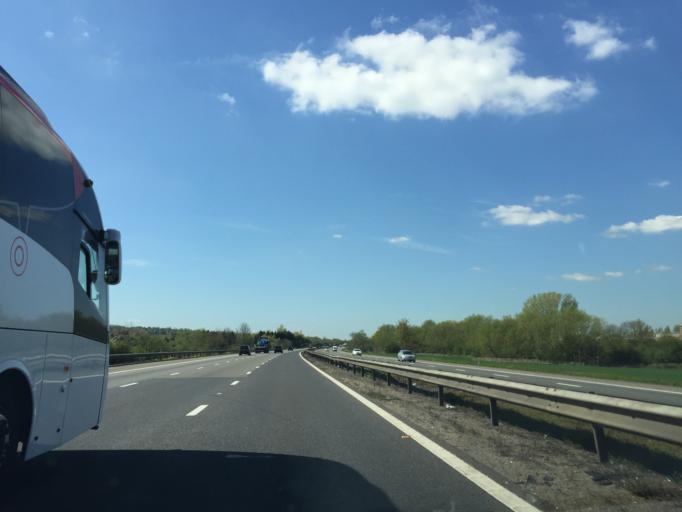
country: GB
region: England
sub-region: Essex
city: Theydon Bois
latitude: 51.6500
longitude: 0.0990
